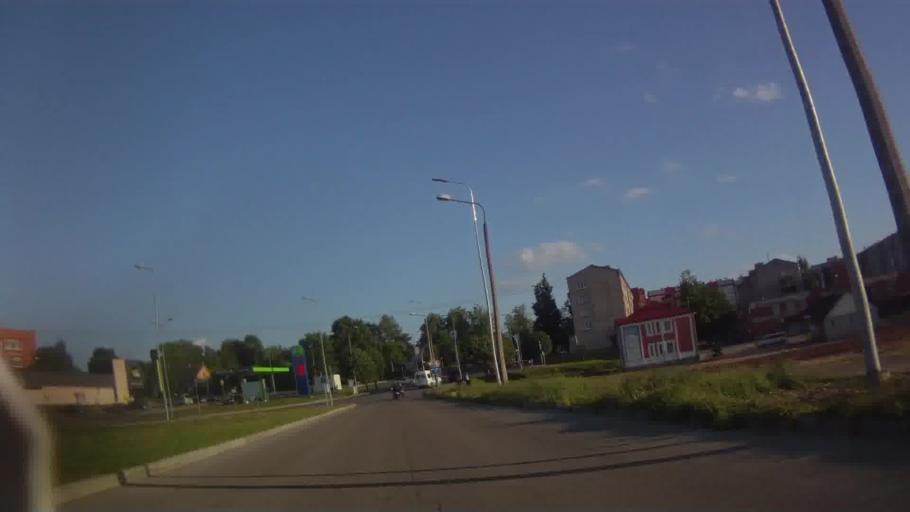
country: LV
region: Rezekne
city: Rezekne
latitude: 56.5172
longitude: 27.3366
